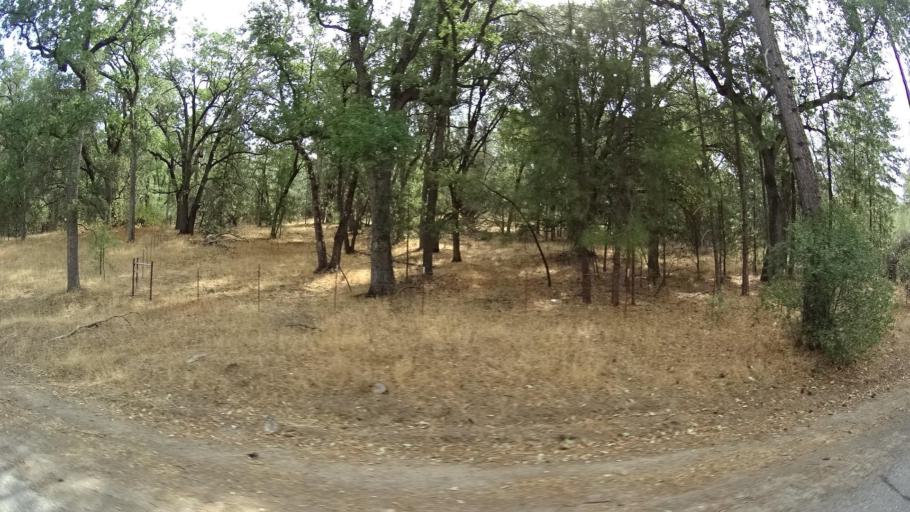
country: US
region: California
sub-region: Mariposa County
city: Midpines
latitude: 37.5113
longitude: -119.8803
